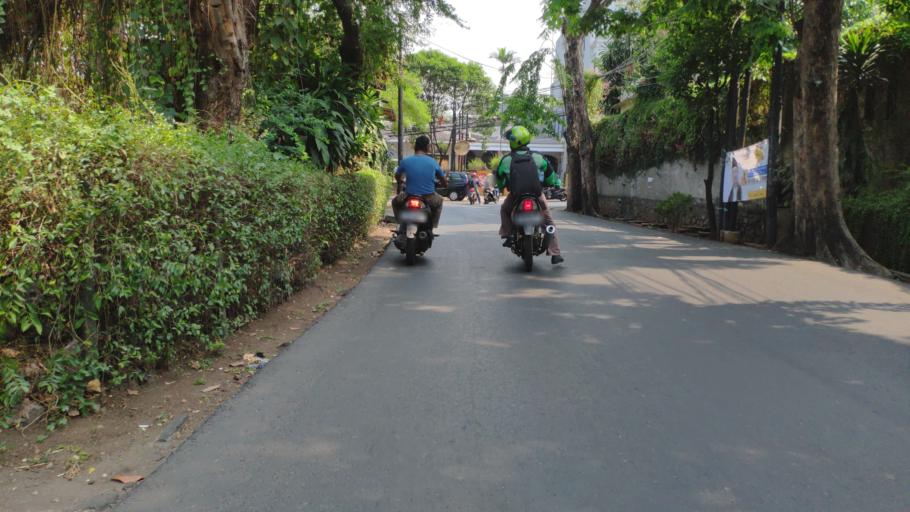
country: ID
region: Jakarta Raya
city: Jakarta
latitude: -6.2577
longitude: 106.8245
